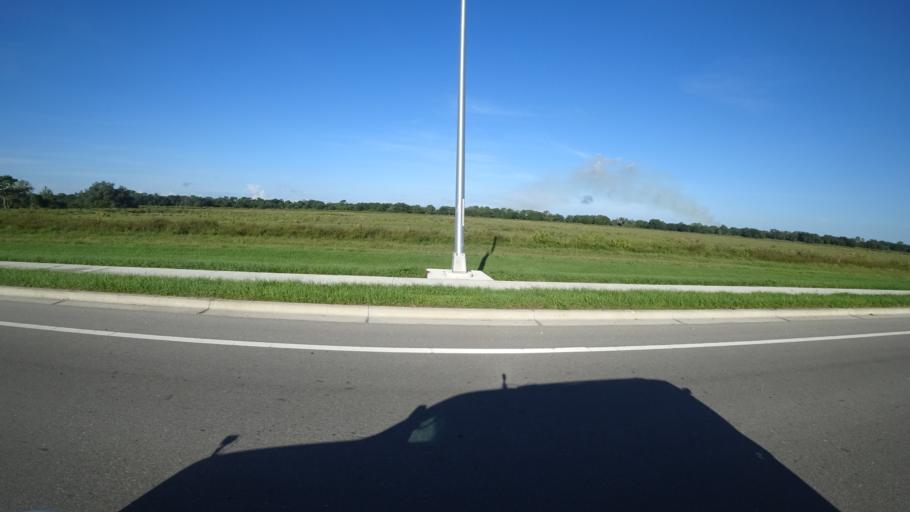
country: US
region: Florida
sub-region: Sarasota County
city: The Meadows
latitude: 27.4355
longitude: -82.3733
